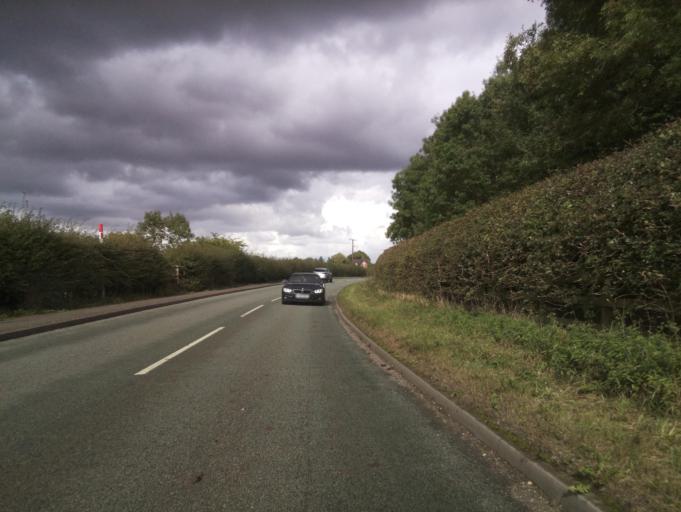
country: GB
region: England
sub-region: Staffordshire
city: Eccleshall
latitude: 52.8818
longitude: -2.2358
